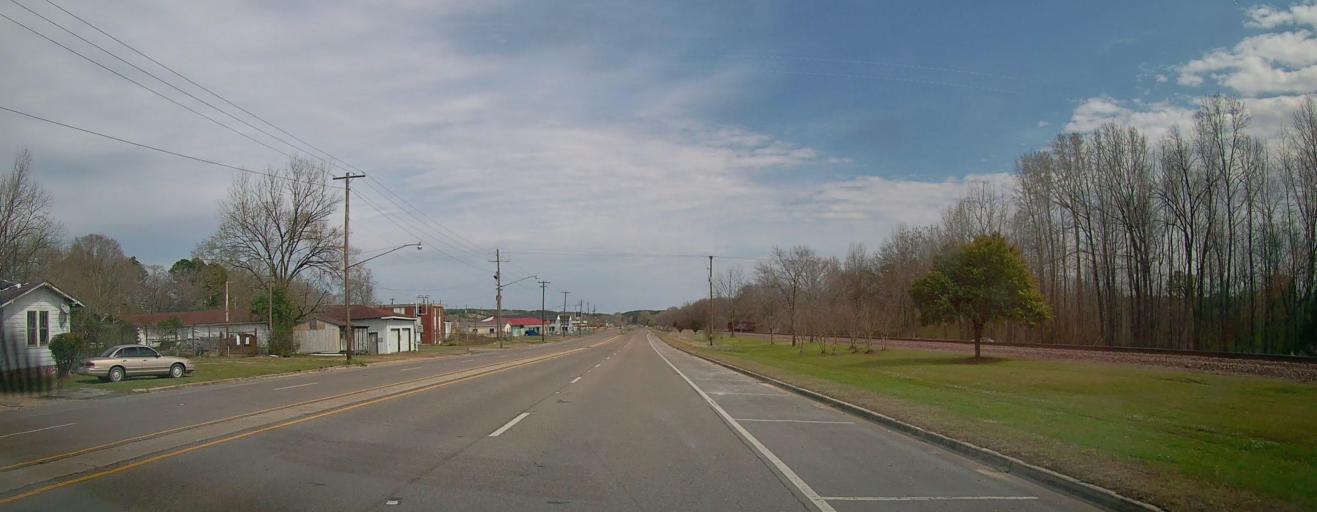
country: US
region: Alabama
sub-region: Walker County
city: Carbon Hill
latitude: 33.8875
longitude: -87.5261
